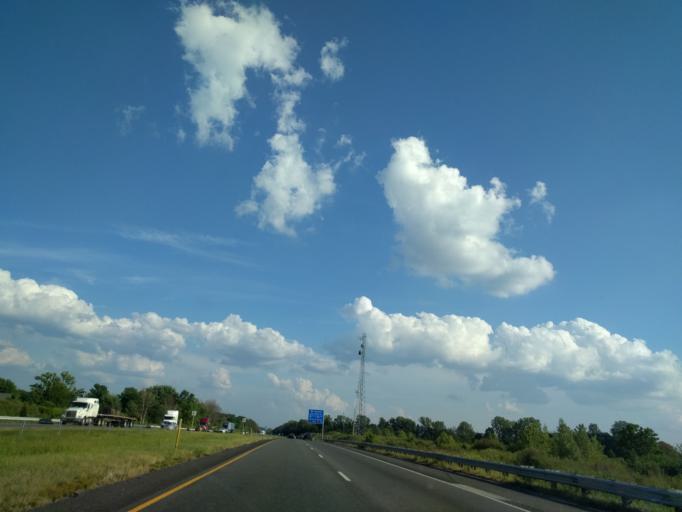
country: US
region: Indiana
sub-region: Boone County
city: Zionsville
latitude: 39.9204
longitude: -86.3305
